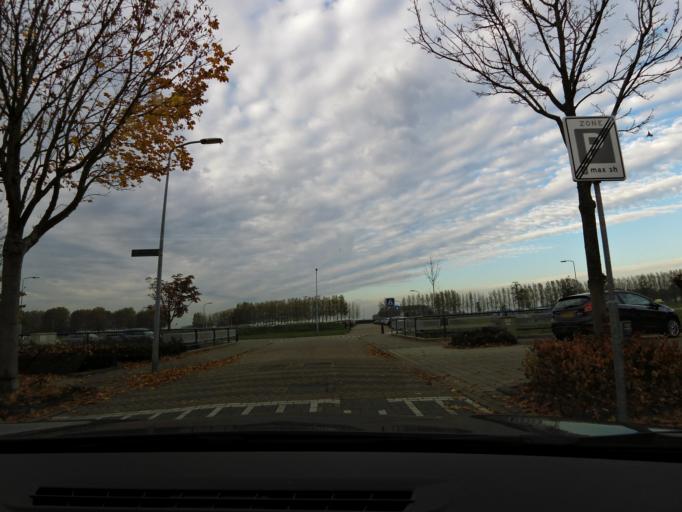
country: NL
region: South Holland
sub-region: Gemeente Goeree-Overflakkee
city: Dirksland
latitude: 51.7524
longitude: 4.0995
